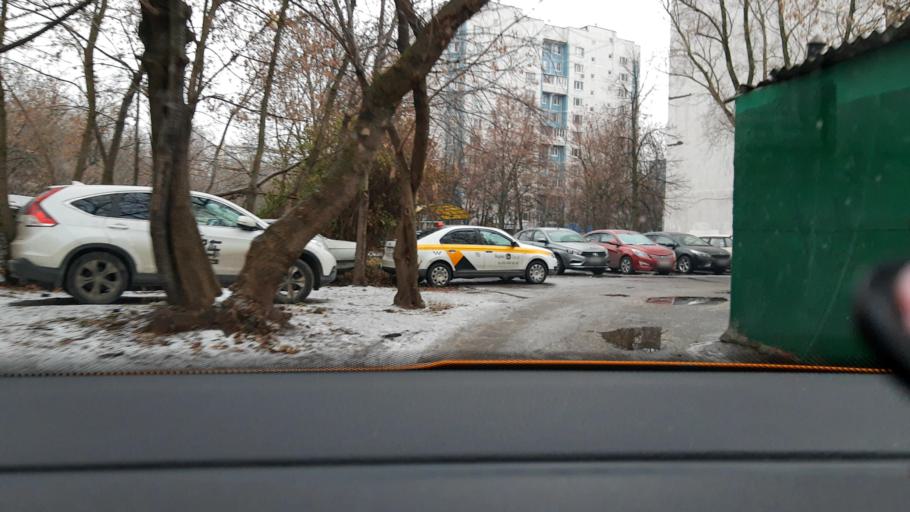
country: RU
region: Moscow
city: Shchukino
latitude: 55.7981
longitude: 37.4594
